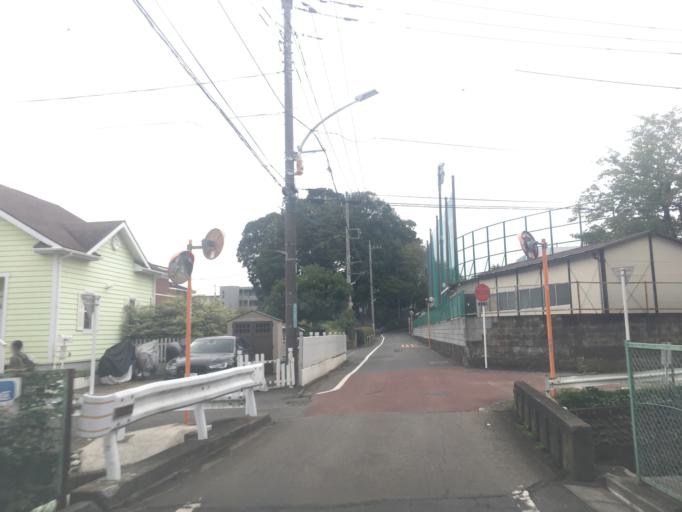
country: JP
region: Tokyo
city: Higashimurayama-shi
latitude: 35.7594
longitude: 139.4595
